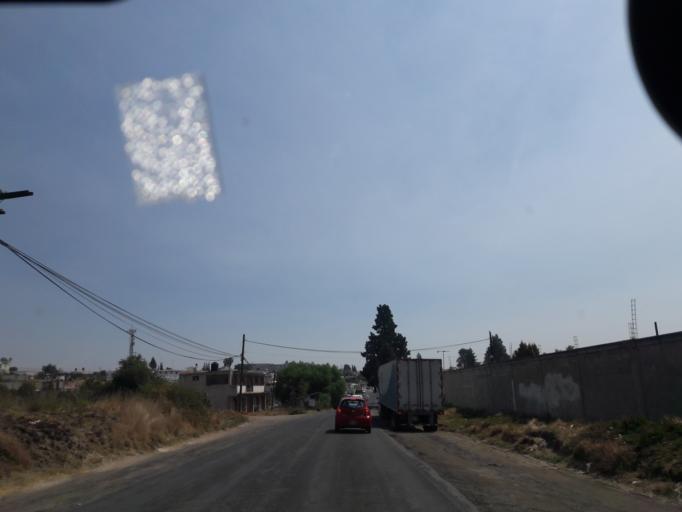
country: MX
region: Tlaxcala
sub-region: Ixtacuixtla de Mariano Matamoros
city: Villa Mariano Matamoros
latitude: 19.3124
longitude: -98.3926
